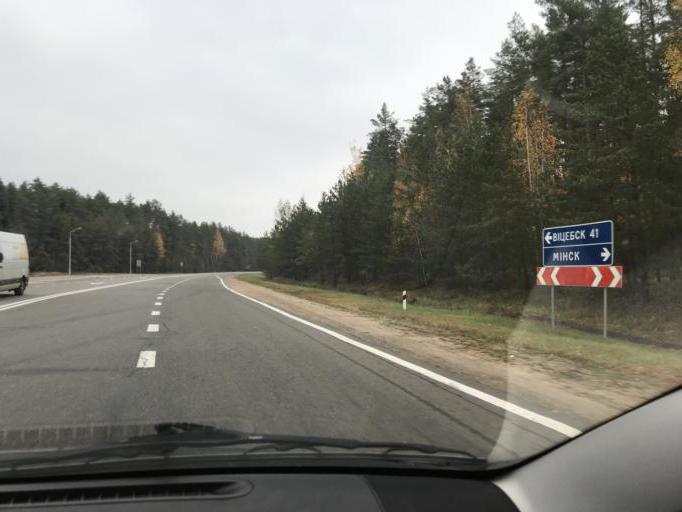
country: BY
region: Vitebsk
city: Syanno
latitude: 55.0633
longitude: 29.5279
